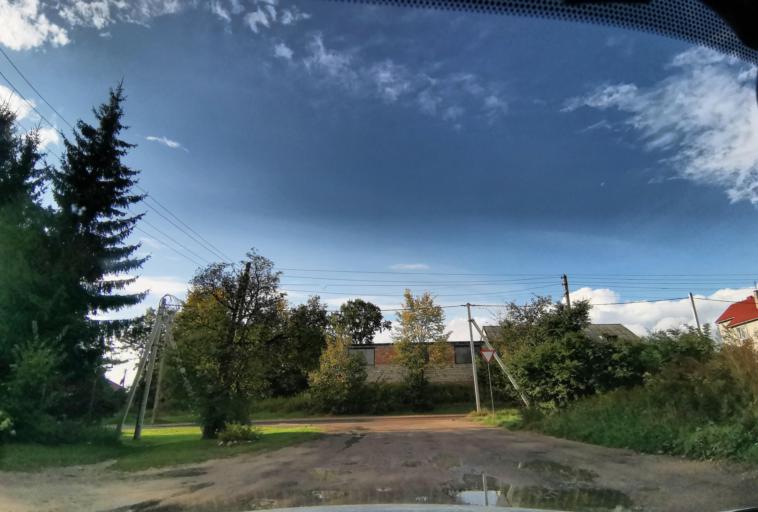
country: RU
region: Kaliningrad
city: Chernyakhovsk
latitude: 54.6586
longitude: 21.8323
